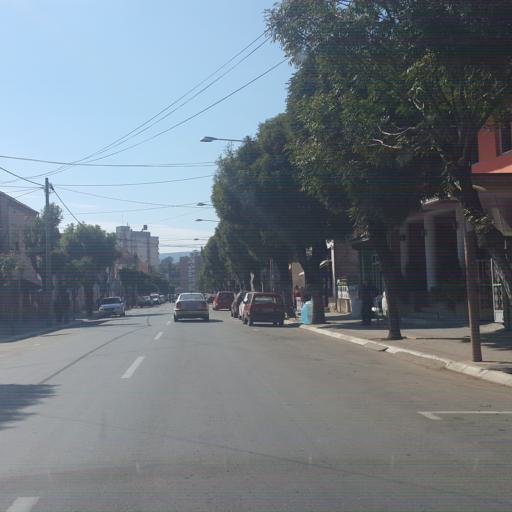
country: RS
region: Central Serbia
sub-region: Zajecarski Okrug
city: Knjazevac
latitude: 43.5704
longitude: 22.2619
